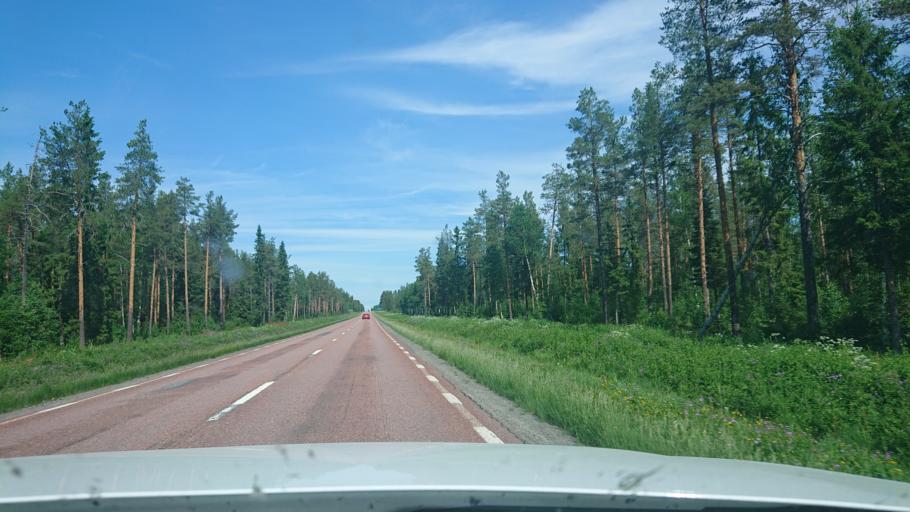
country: SE
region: Jaemtland
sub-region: Stroemsunds Kommun
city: Stroemsund
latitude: 63.7581
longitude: 15.4994
